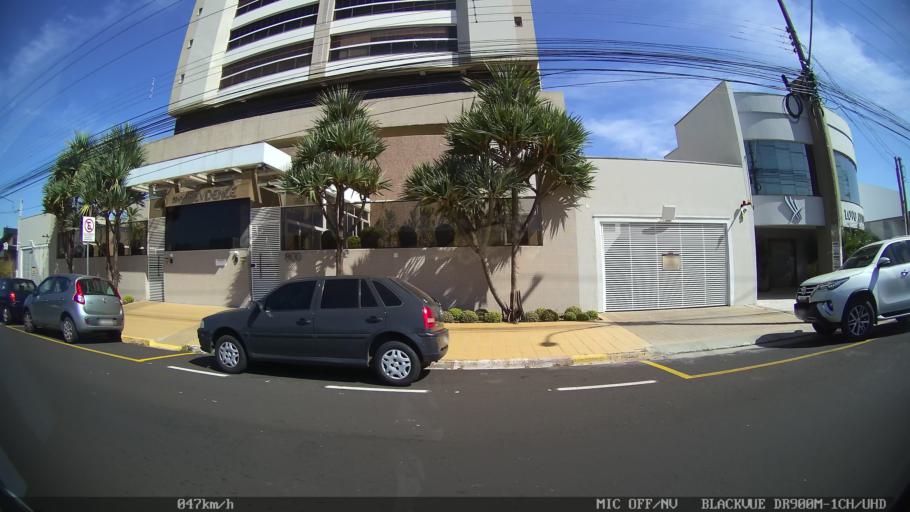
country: BR
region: Sao Paulo
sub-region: Franca
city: Franca
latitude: -20.5478
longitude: -47.4183
